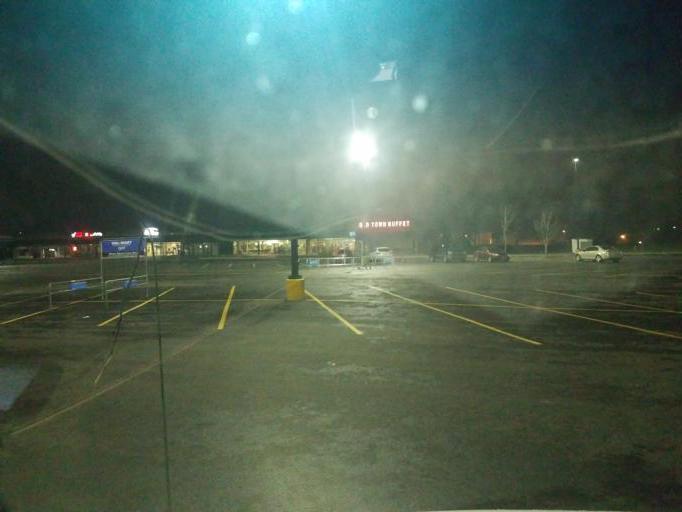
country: US
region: Ohio
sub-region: Williams County
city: Bryan
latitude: 41.4605
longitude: -84.5485
